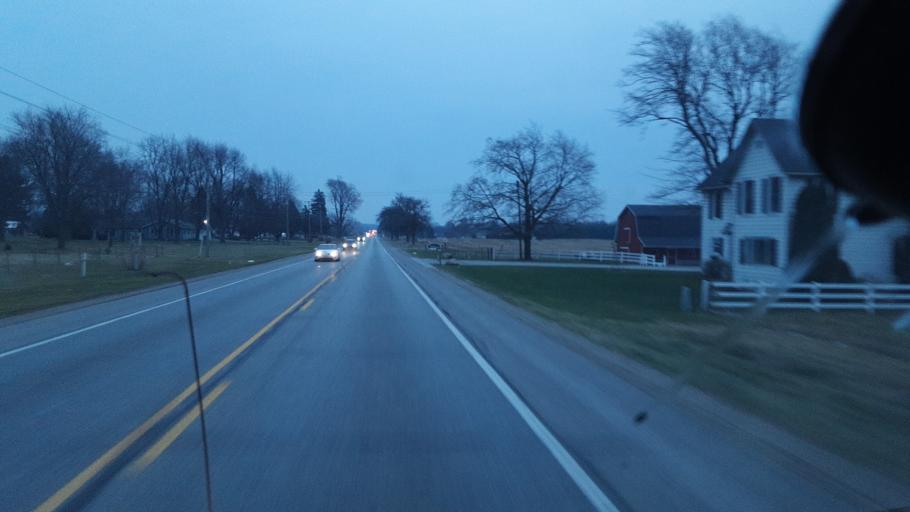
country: US
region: Indiana
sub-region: Elkhart County
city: Middlebury
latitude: 41.6679
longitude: -85.7488
